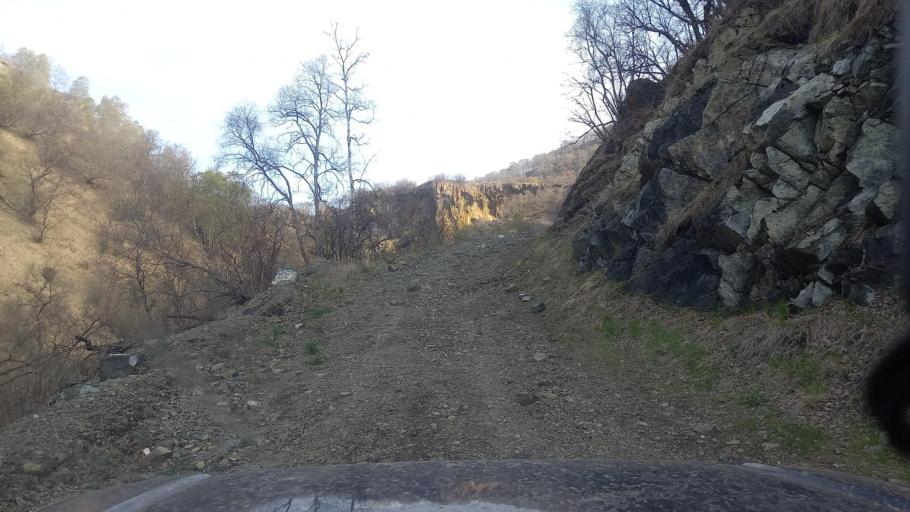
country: RU
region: Kabardino-Balkariya
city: Kamennomostskoye
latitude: 43.6944
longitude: 42.8448
